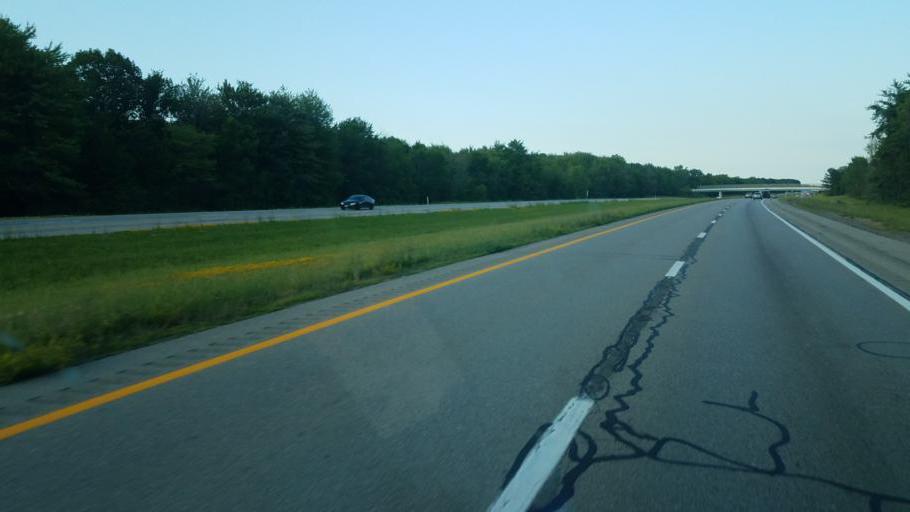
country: US
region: Ohio
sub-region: Ashtabula County
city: Geneva
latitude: 41.7678
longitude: -80.9834
